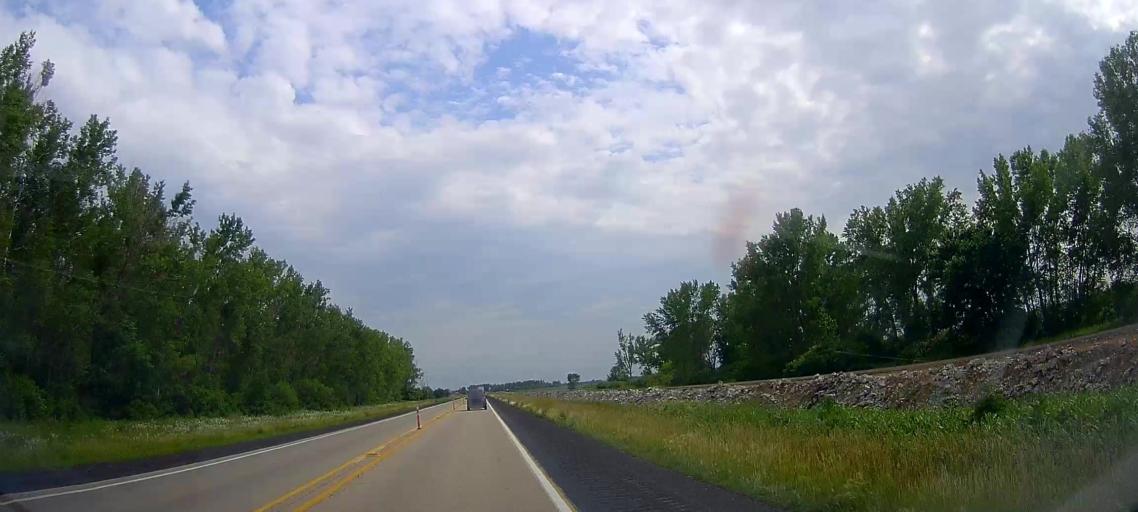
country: US
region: Nebraska
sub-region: Washington County
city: Blair
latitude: 41.6977
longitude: -96.0427
